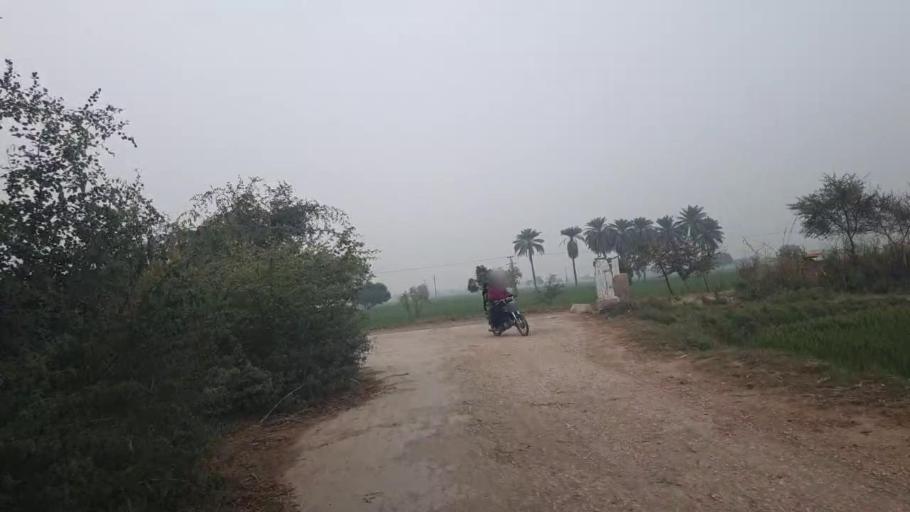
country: PK
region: Sindh
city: Tando Adam
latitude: 25.7701
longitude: 68.7025
